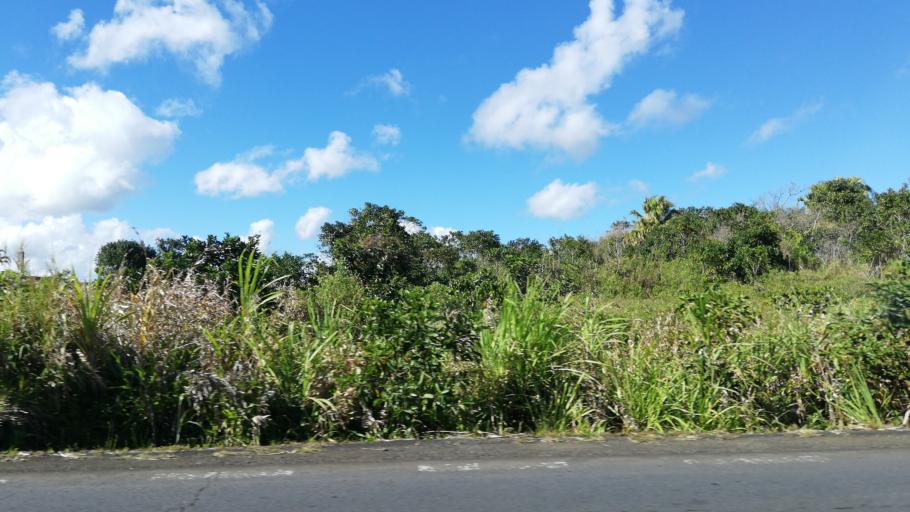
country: MU
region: Moka
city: La Dagotiere
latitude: -20.2327
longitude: 57.5565
